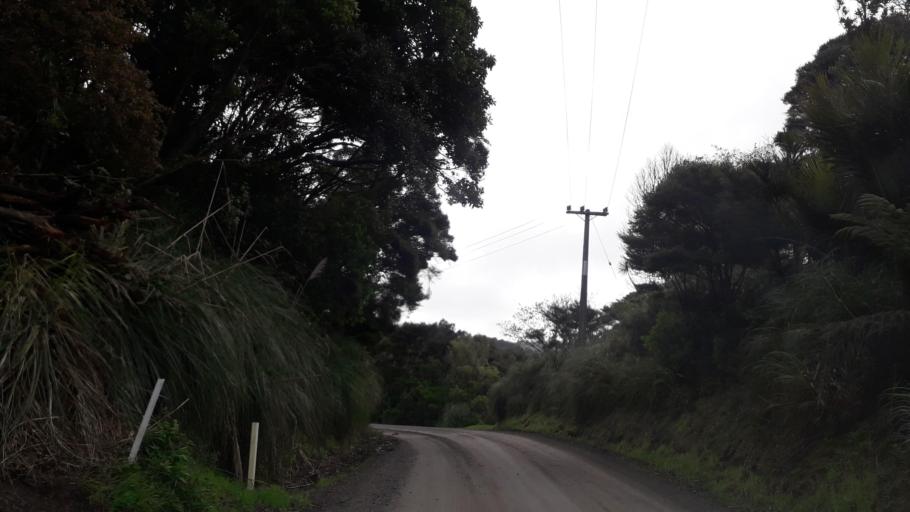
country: NZ
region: Northland
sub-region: Far North District
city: Ahipara
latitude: -35.4394
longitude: 173.3093
